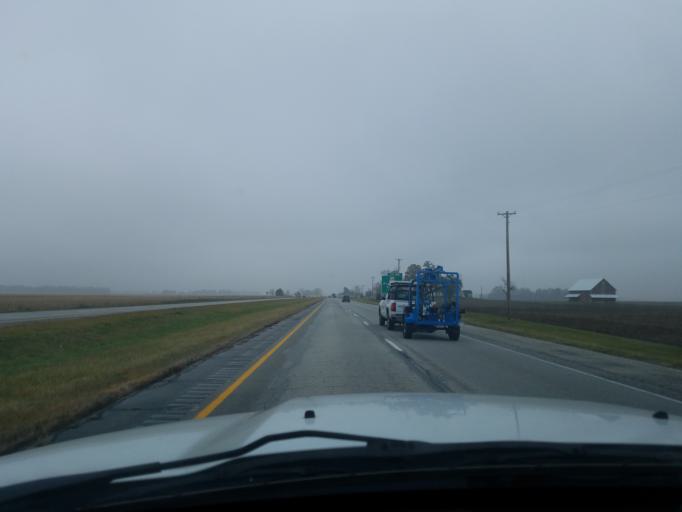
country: US
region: Indiana
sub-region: Tipton County
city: Tipton
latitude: 40.2562
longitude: -86.1273
